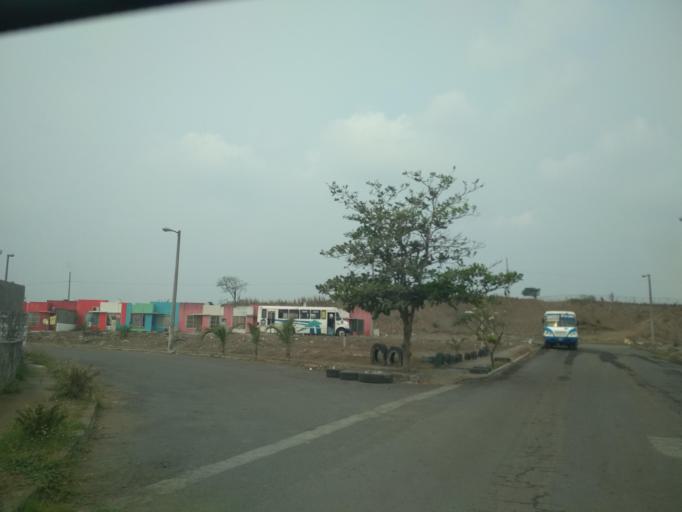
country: MX
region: Veracruz
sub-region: Veracruz
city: Fraccionamiento Geovillas los Pinos
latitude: 19.2318
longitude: -96.2459
